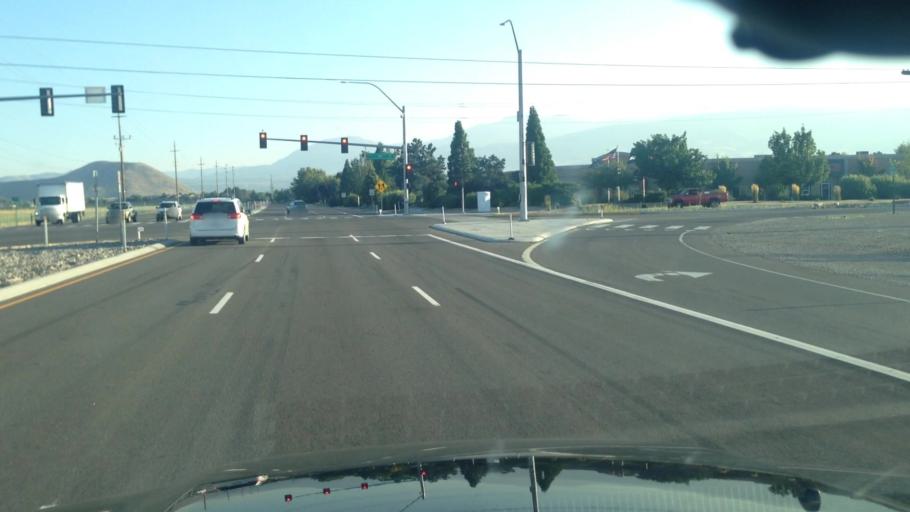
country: US
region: Nevada
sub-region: Washoe County
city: Sparks
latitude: 39.5120
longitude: -119.7442
